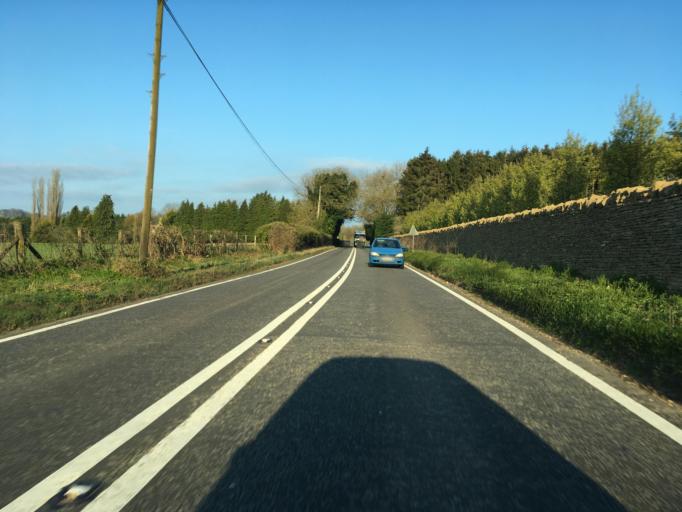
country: GB
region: England
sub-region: Gloucestershire
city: Shipton Village
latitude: 51.8670
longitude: -1.9775
